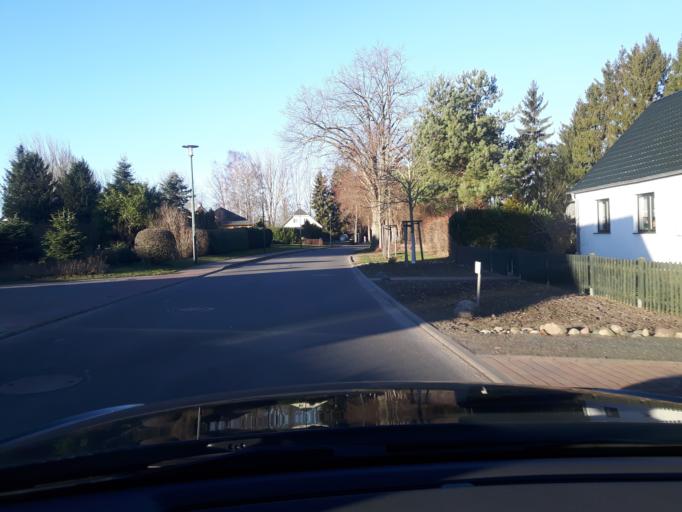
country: DE
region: Mecklenburg-Vorpommern
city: Sehlen
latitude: 54.3801
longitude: 13.3818
